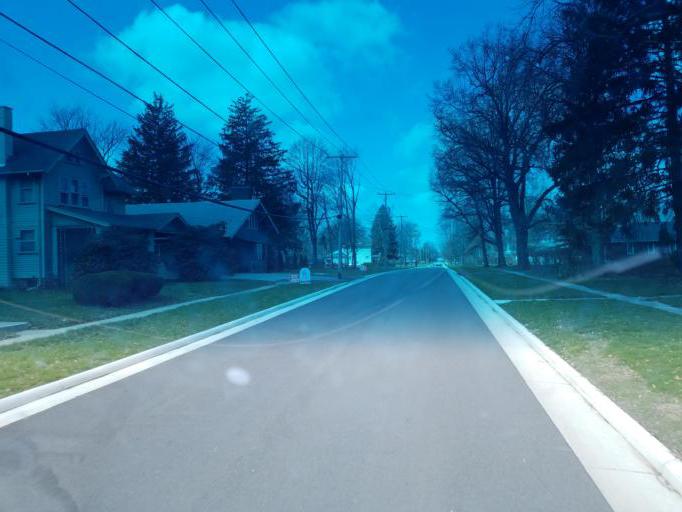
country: US
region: Ohio
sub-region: Crawford County
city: Bucyrus
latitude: 40.7974
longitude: -82.9787
